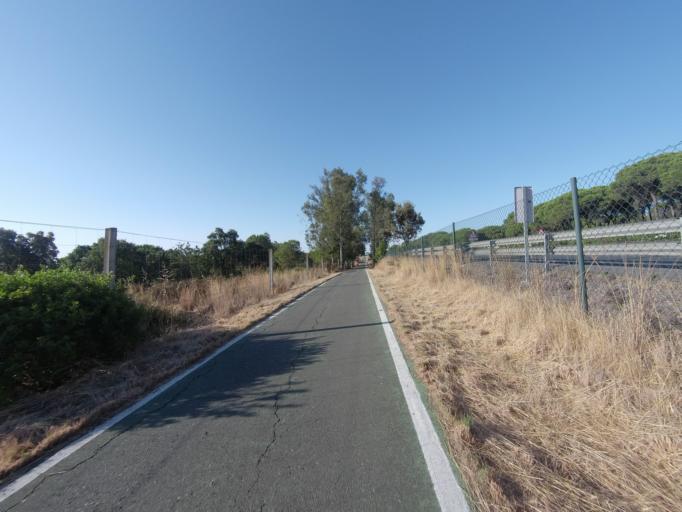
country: ES
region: Andalusia
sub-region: Provincia de Huelva
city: Aljaraque
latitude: 37.2446
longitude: -7.0182
